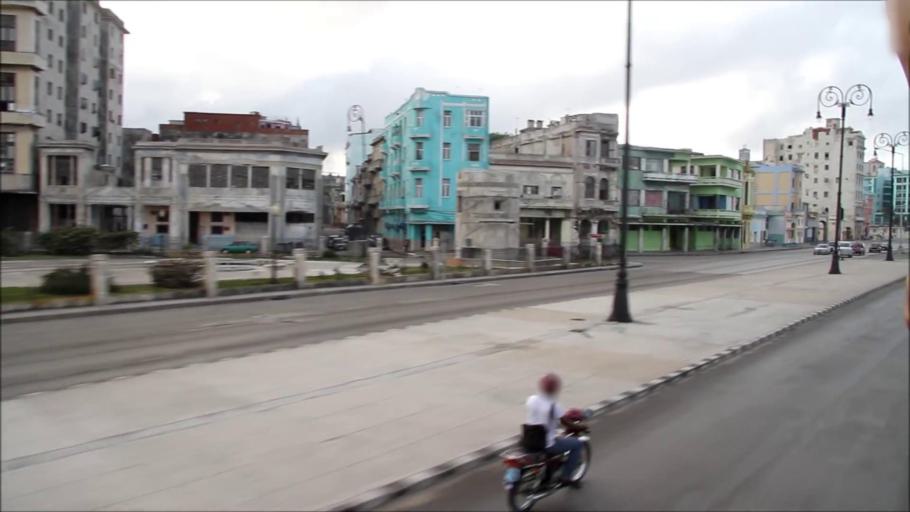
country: CU
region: La Habana
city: Centro Habana
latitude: 23.1417
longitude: -82.3736
